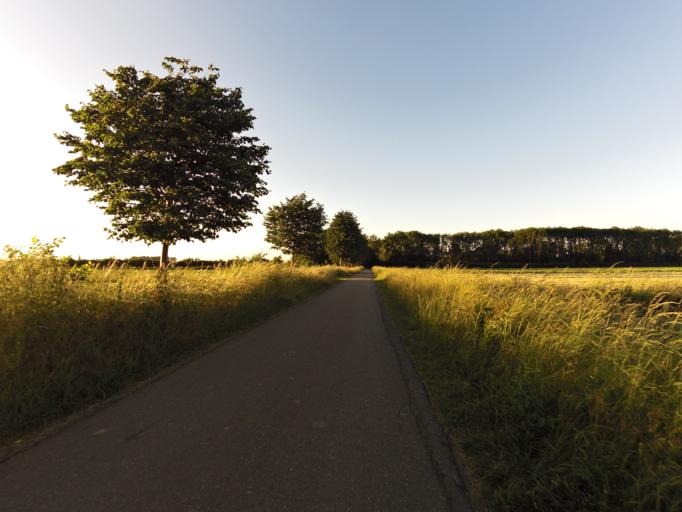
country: NL
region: Gelderland
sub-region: Gemeente Doesburg
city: Doesburg
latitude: 51.9944
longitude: 6.1689
